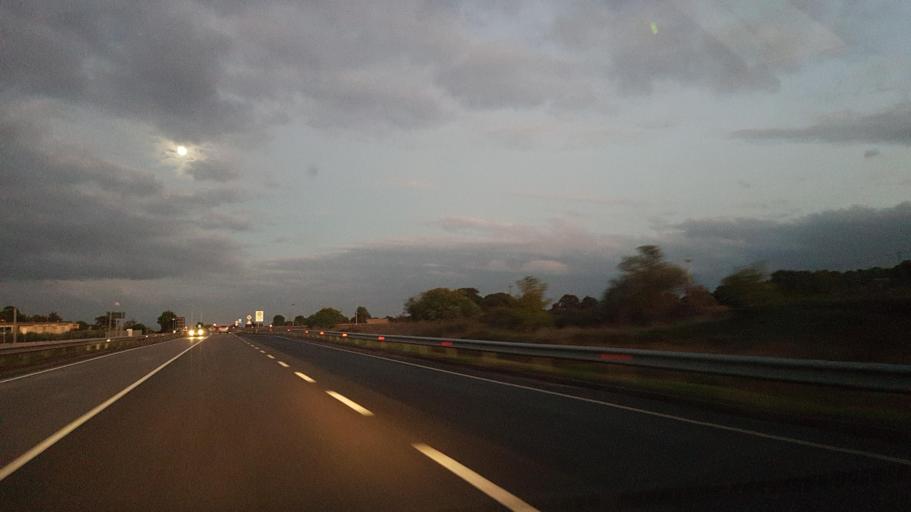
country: IT
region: Apulia
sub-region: Provincia di Taranto
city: Laterza
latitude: 40.6489
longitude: 16.8249
